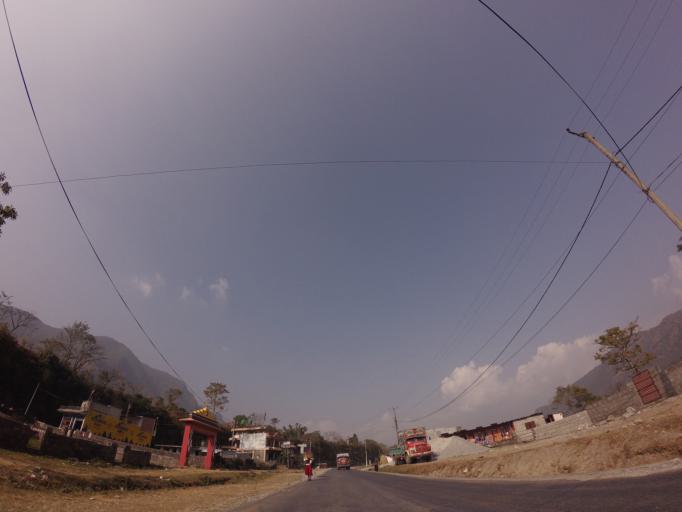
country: NP
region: Western Region
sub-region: Gandaki Zone
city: Pokhara
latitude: 28.2589
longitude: 83.9610
